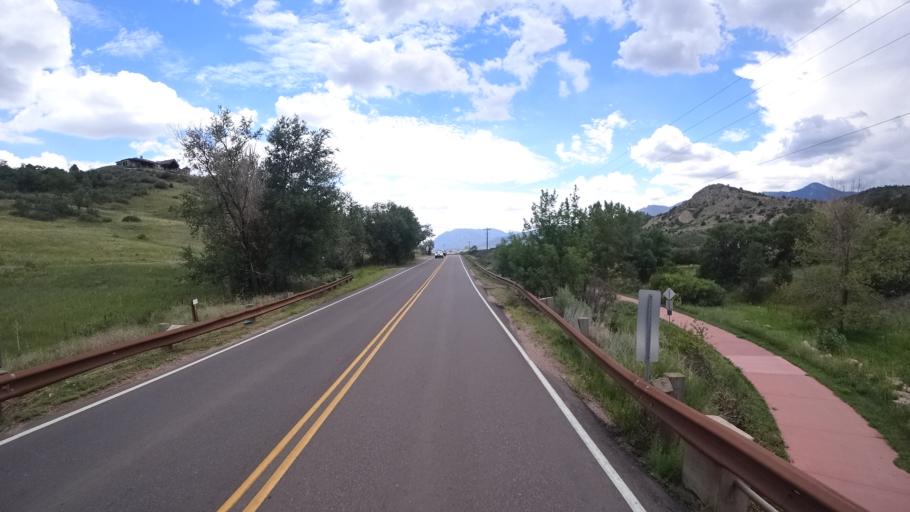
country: US
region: Colorado
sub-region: El Paso County
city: Manitou Springs
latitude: 38.8908
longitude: -104.8752
